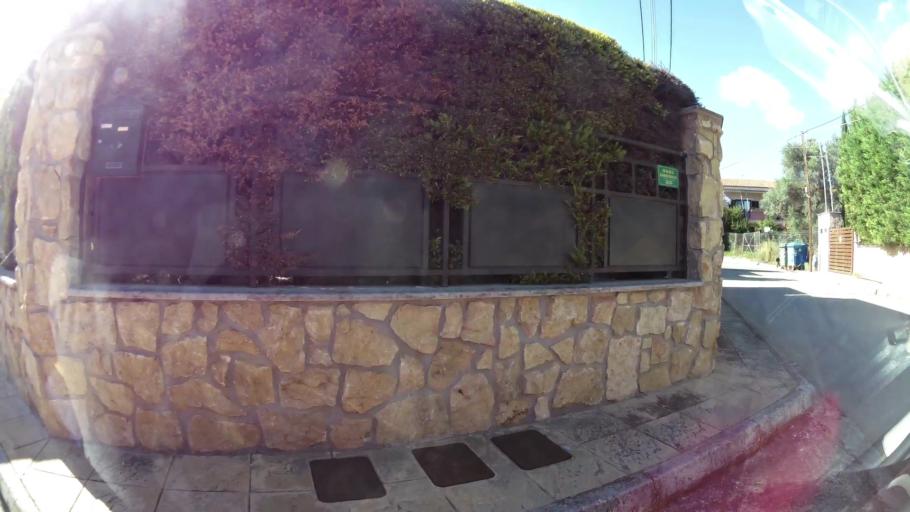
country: GR
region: Attica
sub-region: Nomarchia Anatolikis Attikis
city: Pikermi
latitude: 38.0035
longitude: 23.9384
